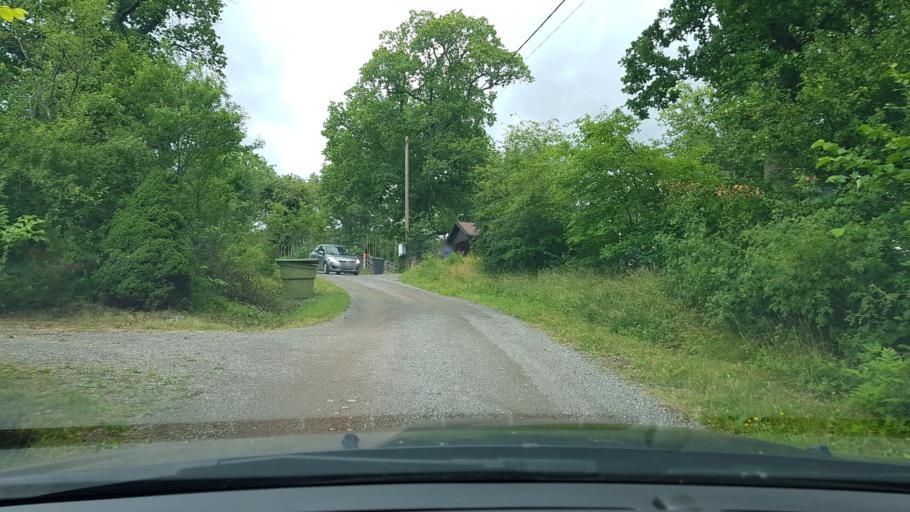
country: SE
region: Uppsala
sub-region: Uppsala Kommun
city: Alsike
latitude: 59.7243
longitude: 17.6889
